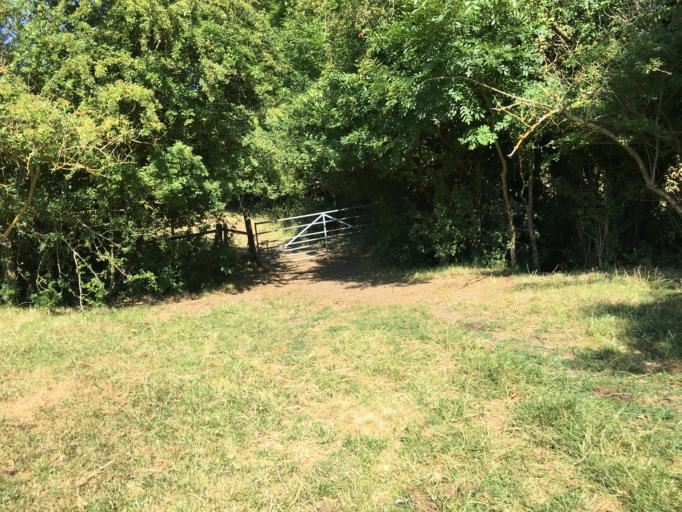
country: GB
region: England
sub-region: Warwickshire
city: Rugby
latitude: 52.4002
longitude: -1.2282
